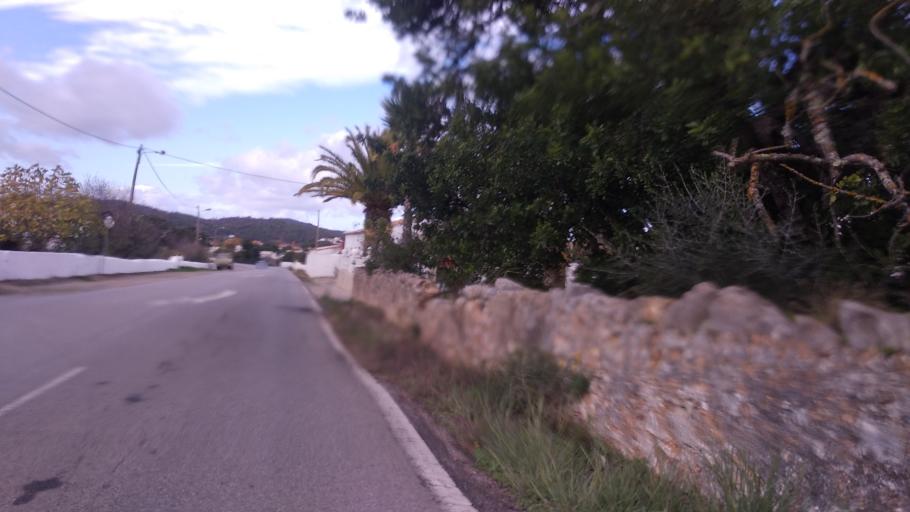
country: PT
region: Faro
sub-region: Sao Bras de Alportel
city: Sao Bras de Alportel
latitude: 37.1655
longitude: -7.9042
